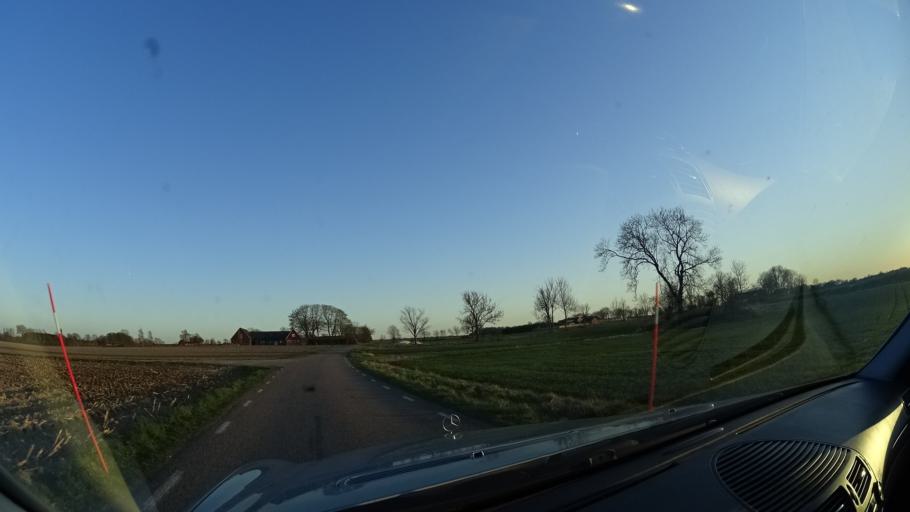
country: SE
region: Skane
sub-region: Eslovs Kommun
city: Stehag
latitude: 55.8609
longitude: 13.4447
